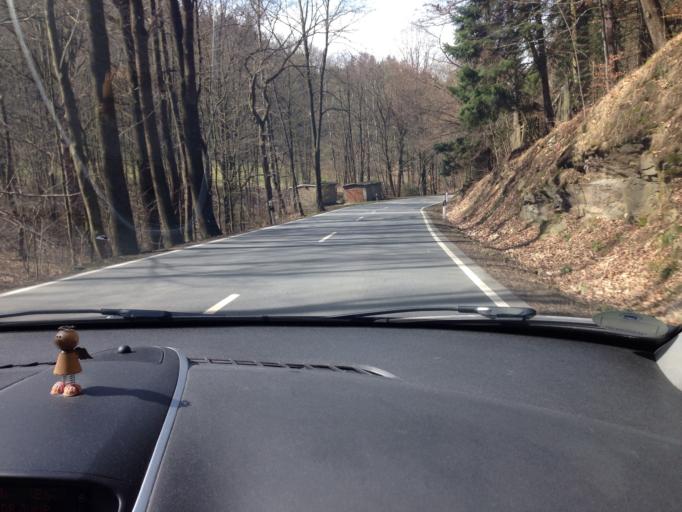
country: DE
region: Saxony
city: Grossolbersdorf
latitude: 50.7010
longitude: 13.0701
